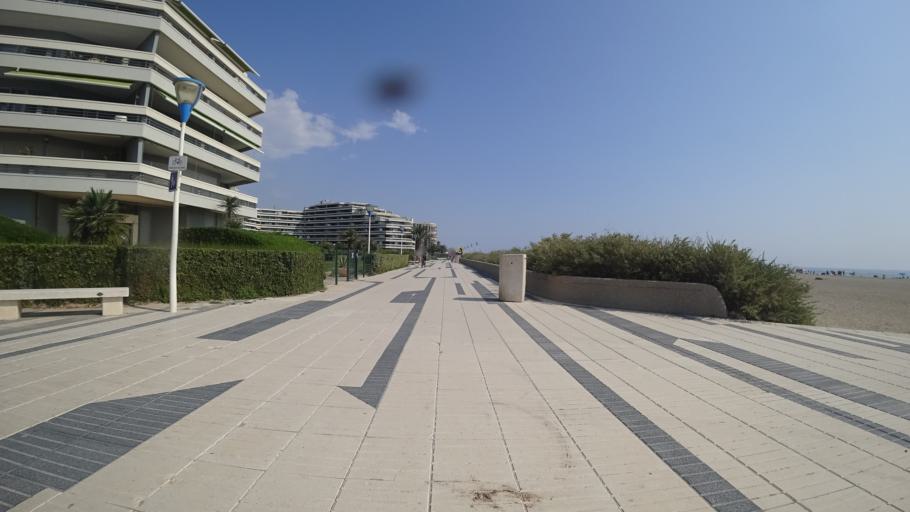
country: FR
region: Languedoc-Roussillon
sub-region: Departement des Pyrenees-Orientales
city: Canet-en-Roussillon
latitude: 42.6768
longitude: 3.0339
